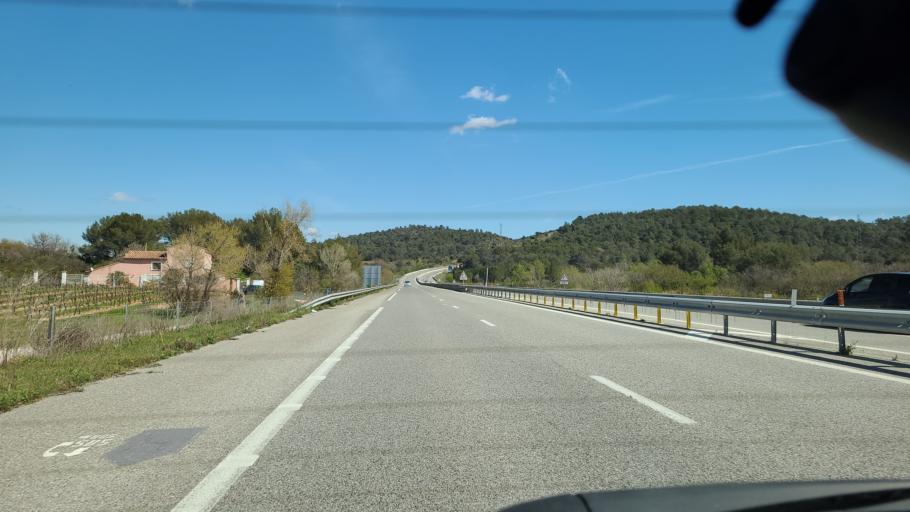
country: FR
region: Provence-Alpes-Cote d'Azur
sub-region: Departement du Var
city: Puget-Ville
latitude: 43.2692
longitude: 6.1612
